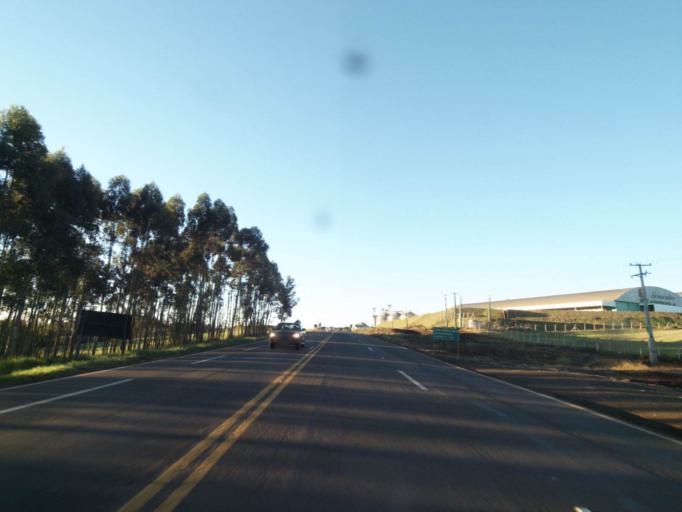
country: BR
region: Parana
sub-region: Faxinal
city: Faxinal
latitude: -23.7096
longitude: -51.1224
